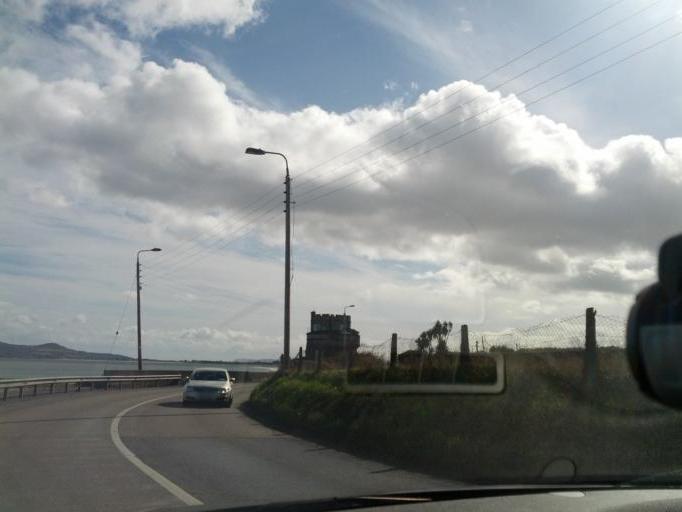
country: IE
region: Leinster
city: Portmarnock
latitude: 53.4372
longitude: -6.1223
